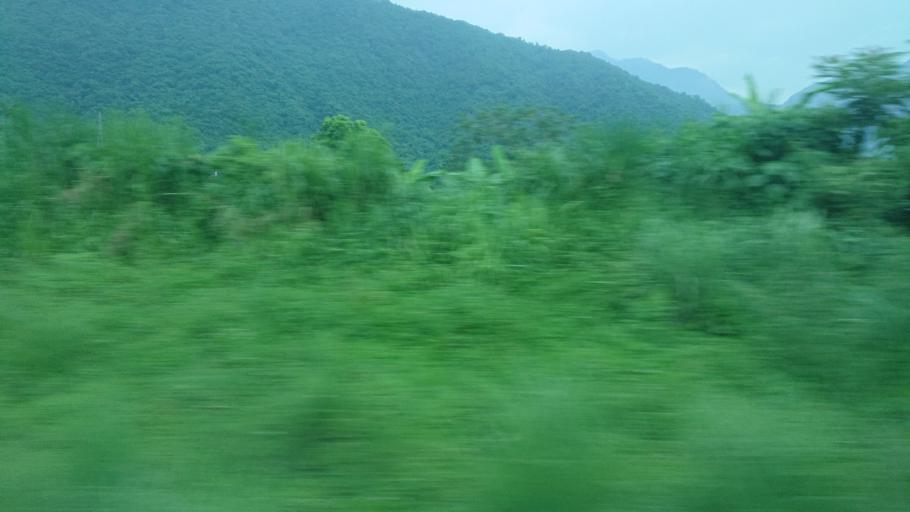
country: TW
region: Taiwan
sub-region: Hualien
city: Hualian
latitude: 24.1208
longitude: 121.6350
